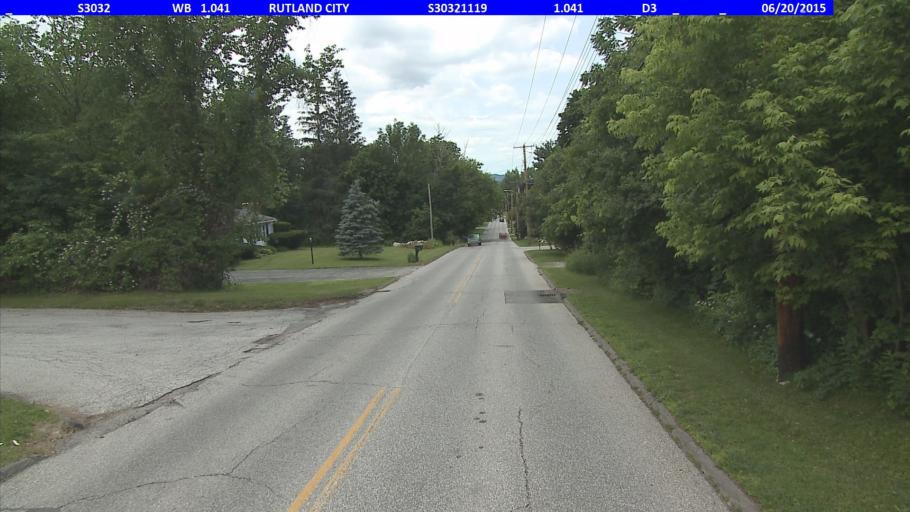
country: US
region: Vermont
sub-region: Rutland County
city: Rutland
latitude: 43.6080
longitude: -72.9520
